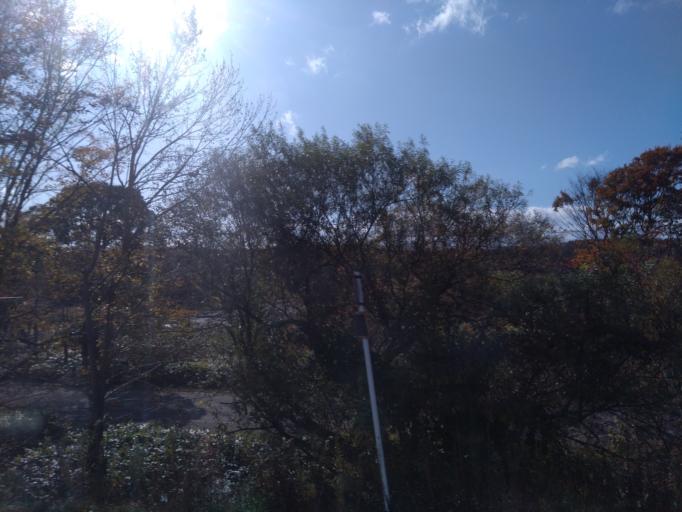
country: JP
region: Hokkaido
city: Kitahiroshima
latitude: 42.9910
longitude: 141.5557
